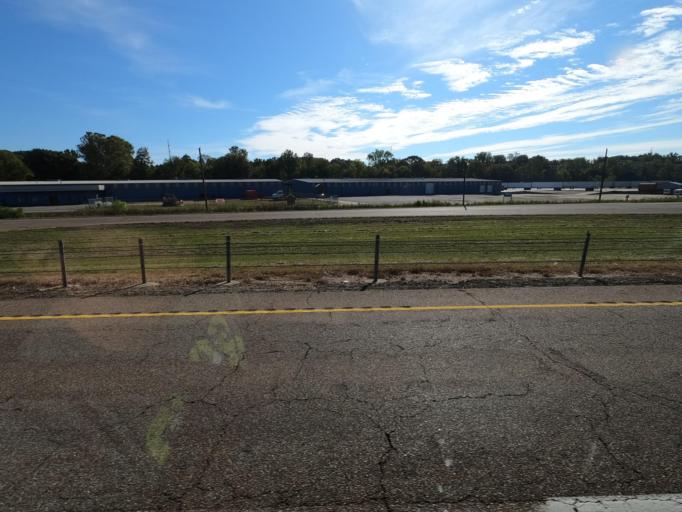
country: US
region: Tennessee
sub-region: Tipton County
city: Brighton
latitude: 35.4943
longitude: -89.7240
